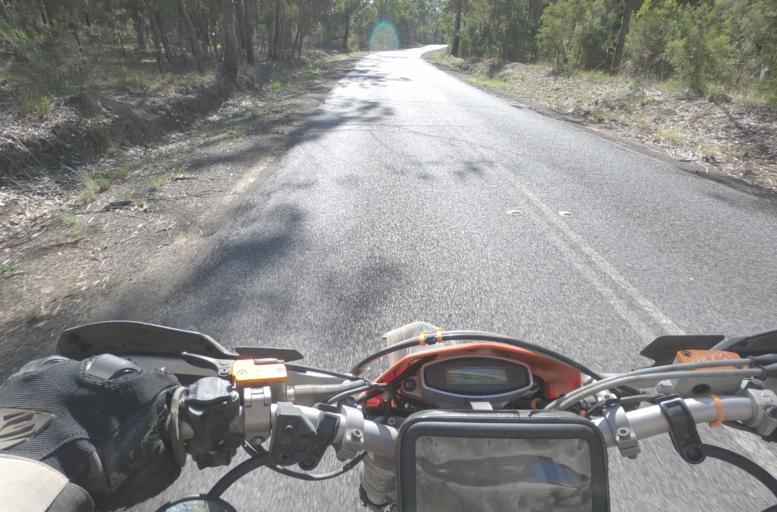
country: AU
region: New South Wales
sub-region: Hawkesbury
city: Scheyville
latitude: -33.5837
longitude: 150.8858
